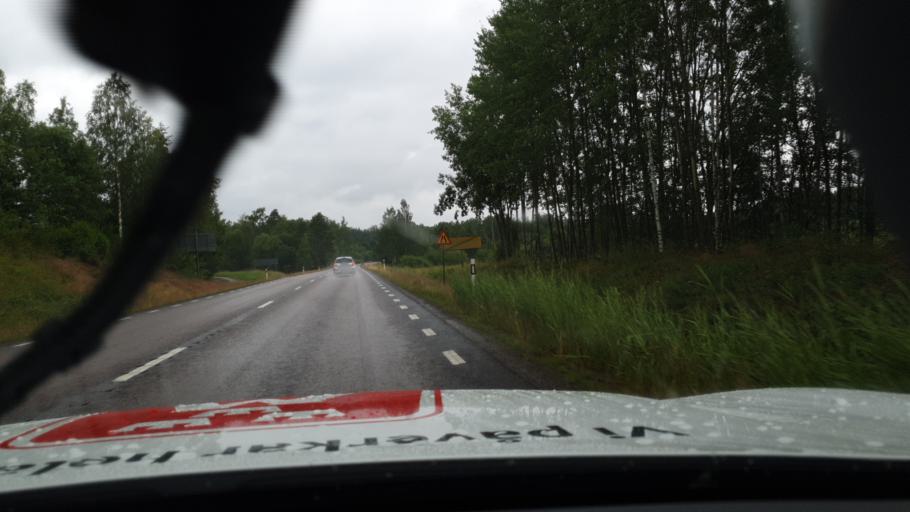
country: SE
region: Vaermland
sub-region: Storfors Kommun
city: Storfors
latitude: 59.4225
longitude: 14.2233
